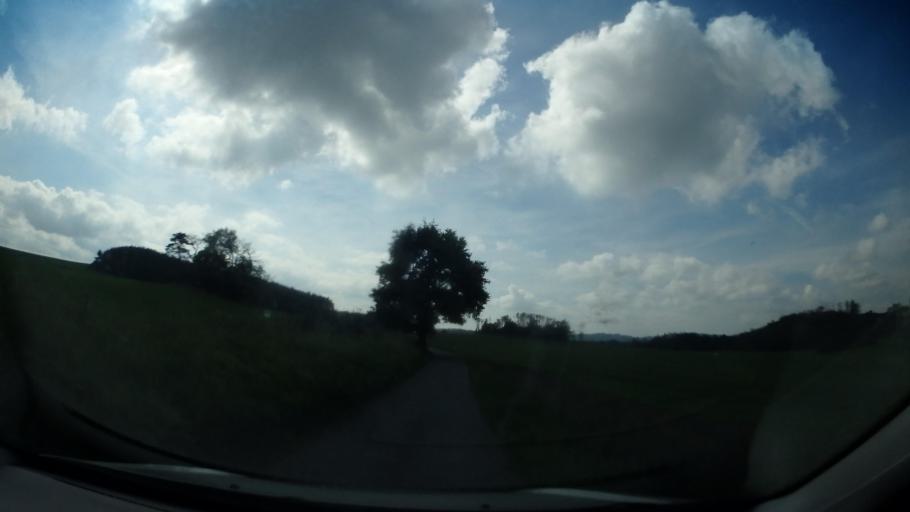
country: CZ
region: Central Bohemia
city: Novy Knin
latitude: 49.7015
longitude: 14.3336
